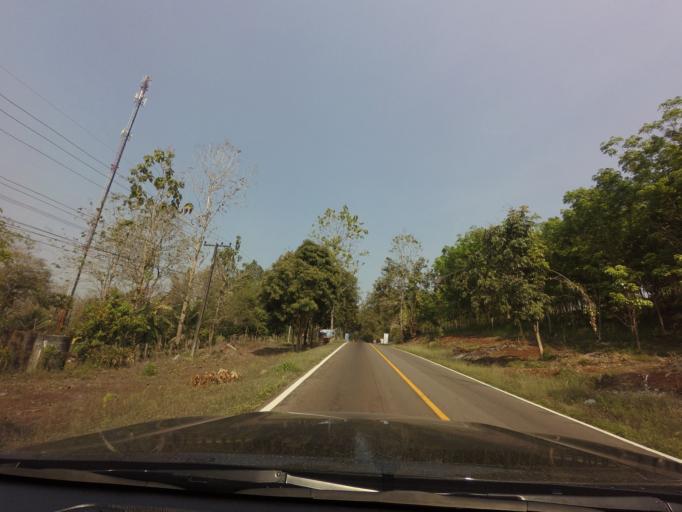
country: TH
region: Kanchanaburi
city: Thong Pha Phum
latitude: 14.7414
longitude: 98.5782
